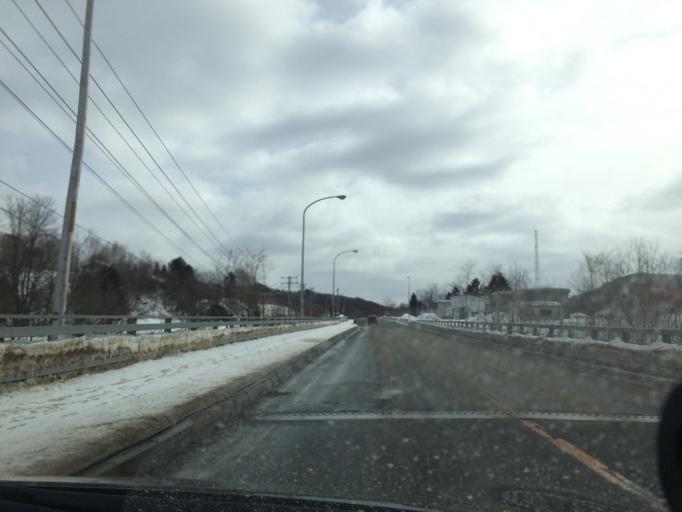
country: JP
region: Hokkaido
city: Iwamizawa
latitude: 42.9553
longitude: 142.0334
